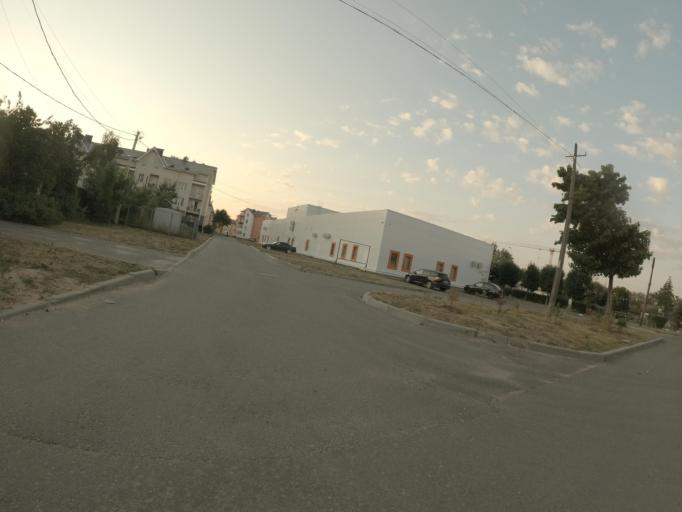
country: RU
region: Leningrad
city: Pavlovo
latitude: 59.8442
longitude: 30.9359
